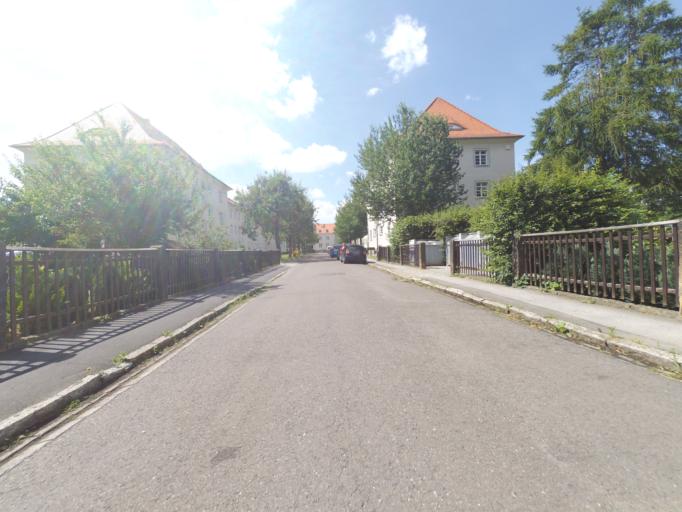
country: DE
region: Saxony
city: Albertstadt
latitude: 51.0349
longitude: 13.7979
